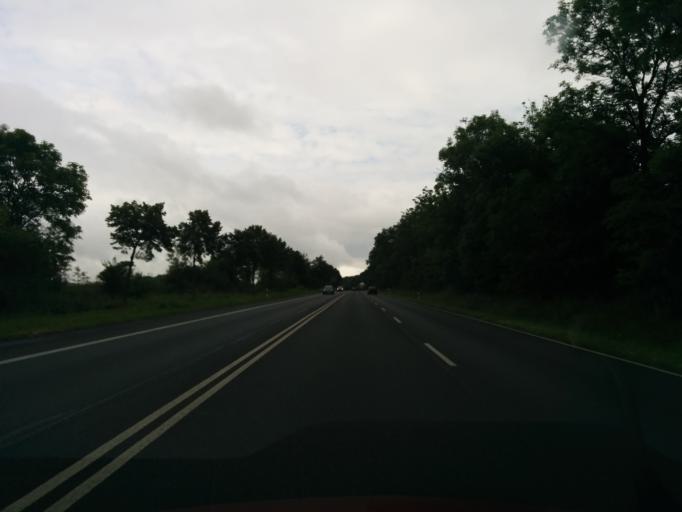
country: DE
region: Lower Saxony
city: Goettingen
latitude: 51.5506
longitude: 9.9925
